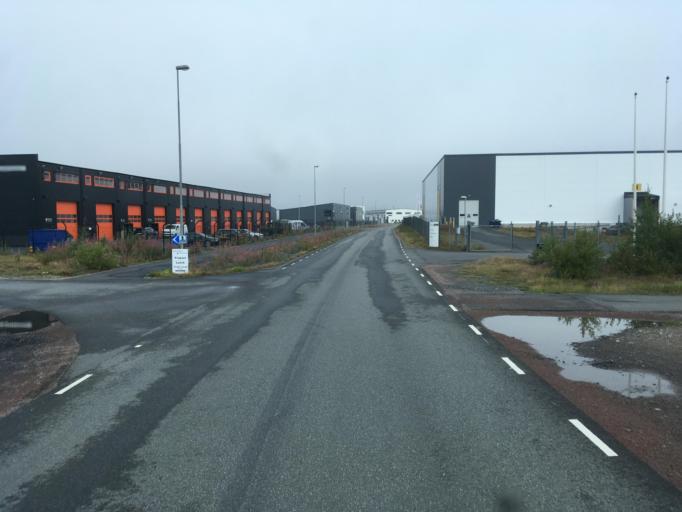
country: SE
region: Joenkoeping
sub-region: Jonkopings Kommun
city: Jonkoping
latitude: 57.7662
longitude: 14.0885
